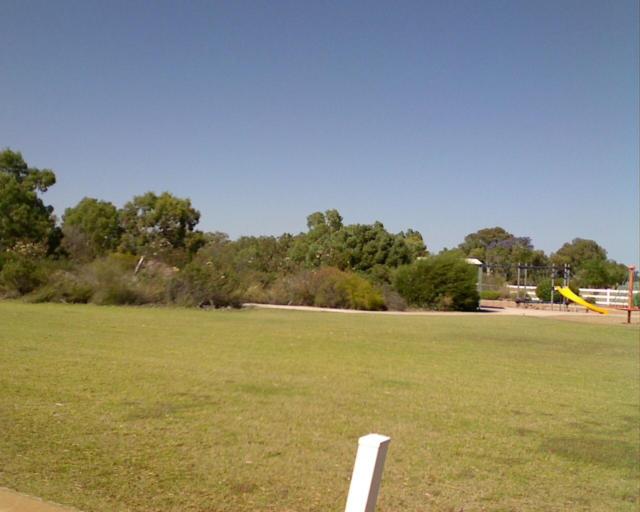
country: AU
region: Western Australia
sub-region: Dandaragan
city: Jurien Bay
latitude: -29.8206
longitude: 115.2657
